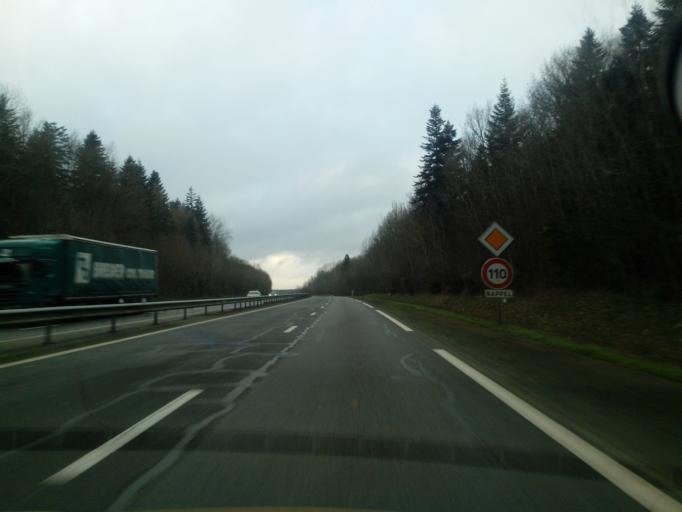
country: FR
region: Brittany
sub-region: Departement d'Ille-et-Vilaine
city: Saint-Meen-le-Grand
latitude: 48.1927
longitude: -2.2157
